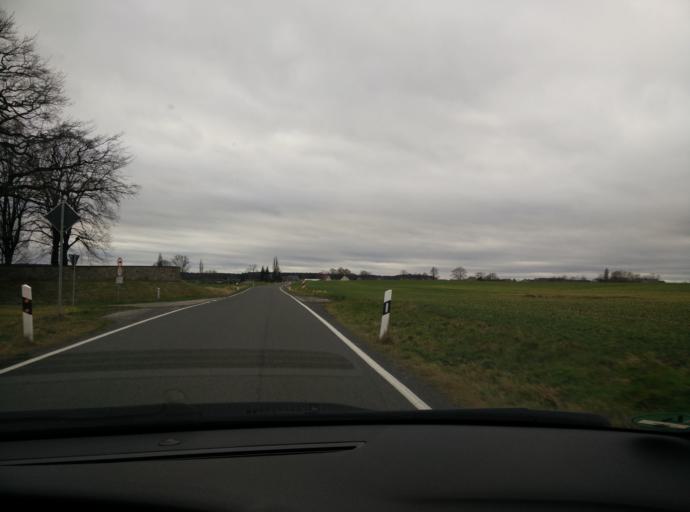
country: DE
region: Saxony
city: Frohburg
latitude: 51.0133
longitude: 12.5691
